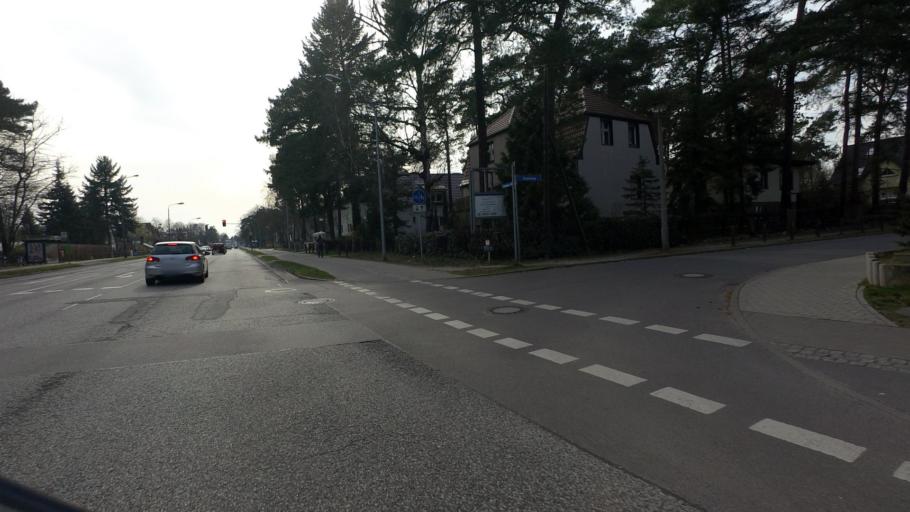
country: DE
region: Brandenburg
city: Stahnsdorf
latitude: 52.3882
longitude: 13.2025
